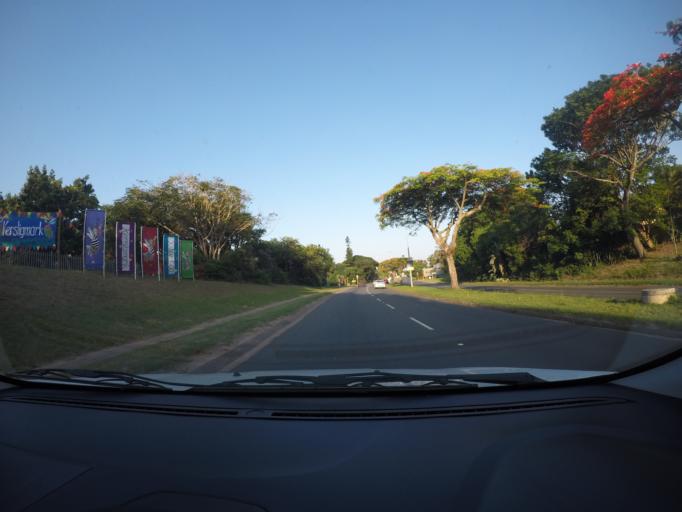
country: ZA
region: KwaZulu-Natal
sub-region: uThungulu District Municipality
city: Richards Bay
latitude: -28.7837
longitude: 32.0962
